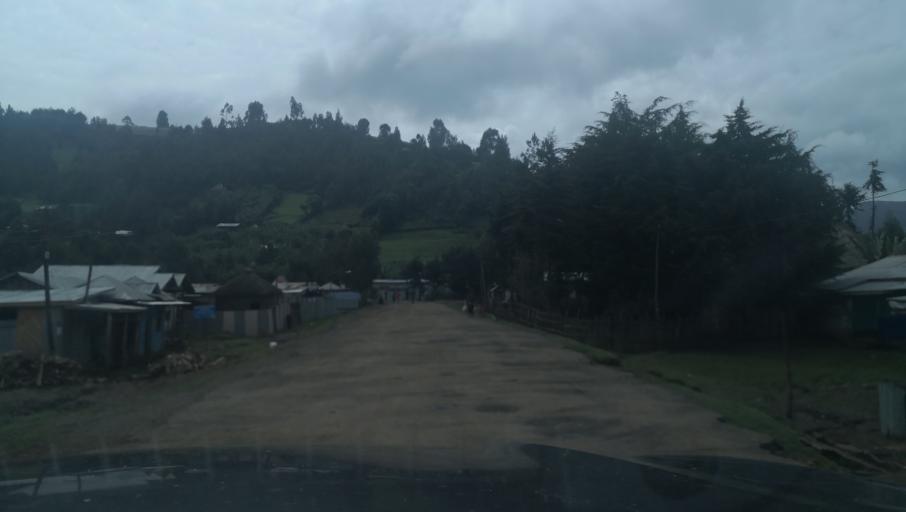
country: ET
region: Southern Nations, Nationalities, and People's Region
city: Butajira
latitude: 8.3209
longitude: 38.3552
